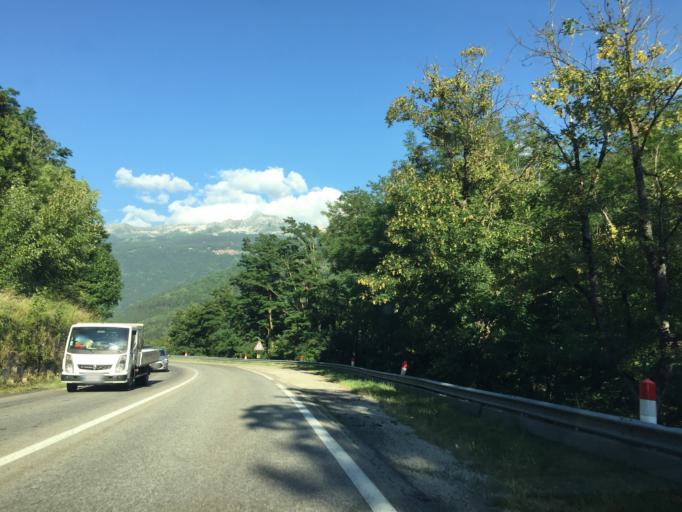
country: FR
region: Rhone-Alpes
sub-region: Departement de la Savoie
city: Macot-la-Plagne
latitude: 45.5670
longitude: 6.6987
